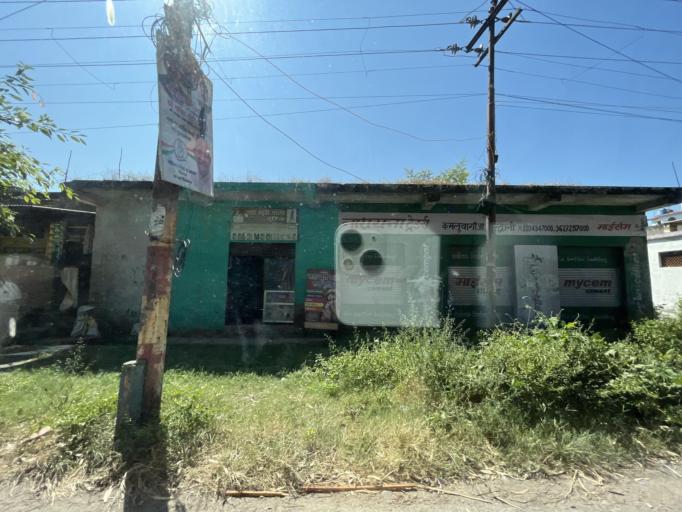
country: IN
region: Uttarakhand
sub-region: Naini Tal
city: Haldwani
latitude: 29.2117
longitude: 79.4603
